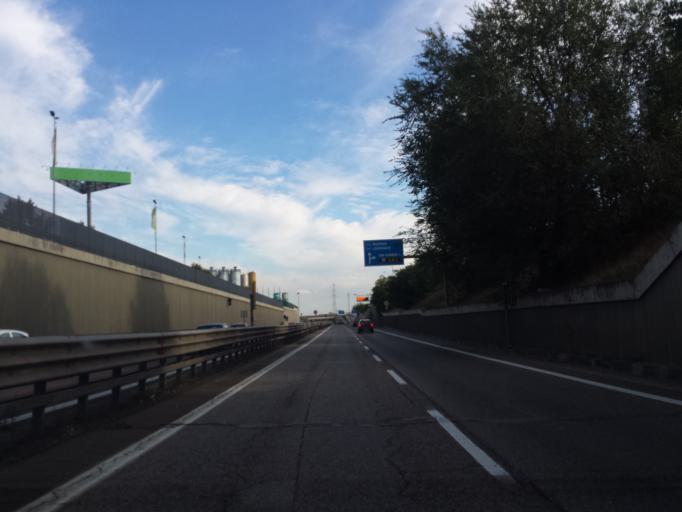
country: IT
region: Veneto
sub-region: Provincia di Verona
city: San Giovanni Lupatoto
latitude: 45.3957
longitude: 11.0160
